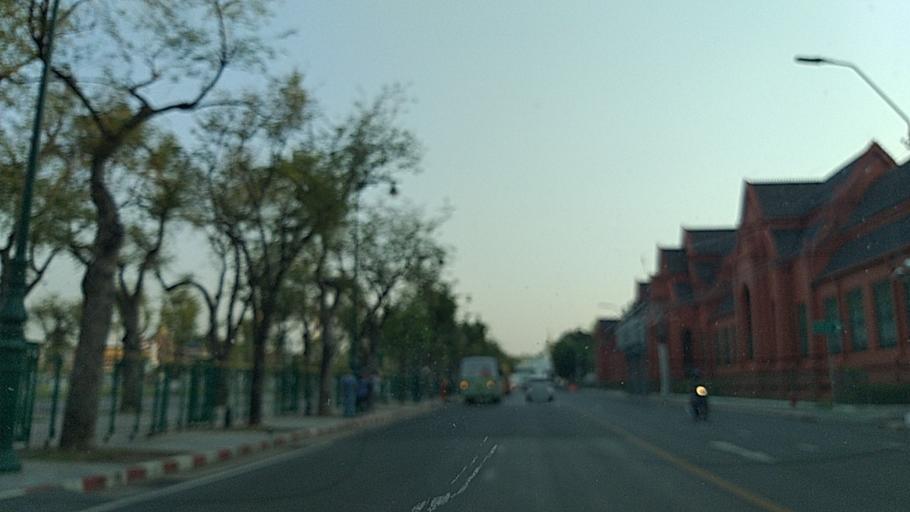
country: TH
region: Bangkok
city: Bangkok
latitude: 13.7549
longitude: 100.4920
